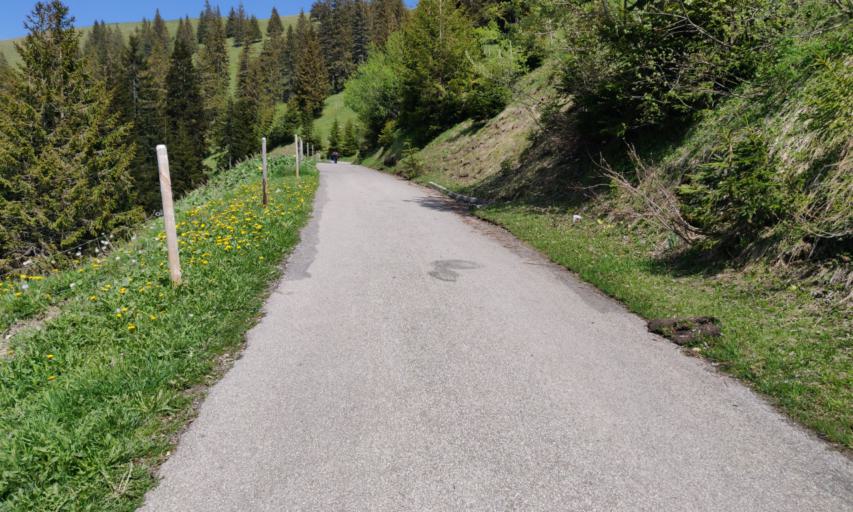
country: CH
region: Fribourg
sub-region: Veveyse District
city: Chatel-Saint-Denis
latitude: 46.5124
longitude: 6.9961
